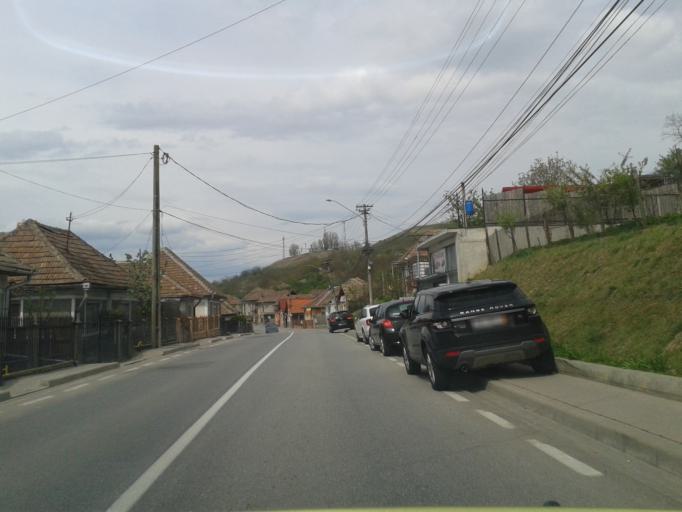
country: RO
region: Alba
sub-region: Municipiul Blaj
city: Veza
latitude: 46.1729
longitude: 23.9406
